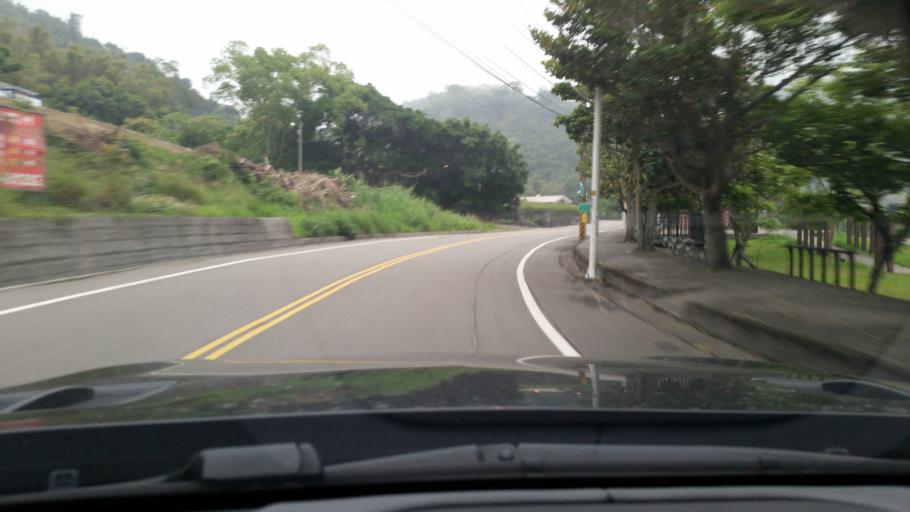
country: TW
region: Taiwan
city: Fengyuan
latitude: 24.3417
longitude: 120.7686
